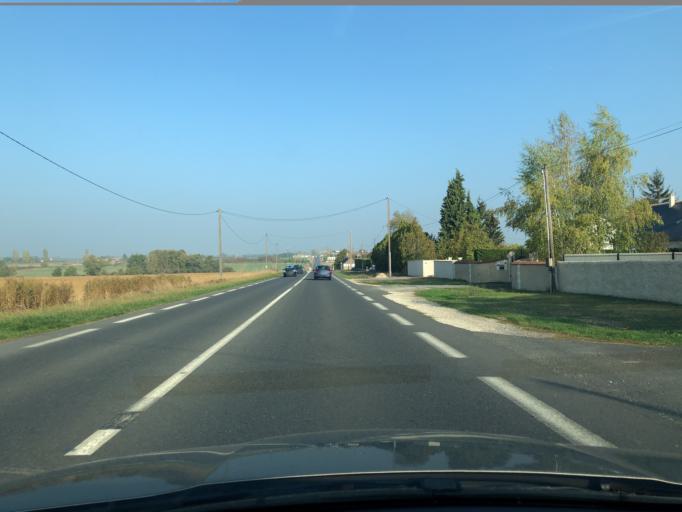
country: FR
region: Centre
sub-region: Departement d'Indre-et-Loire
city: Chanceaux-sur-Choisille
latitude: 47.4520
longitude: 0.6967
